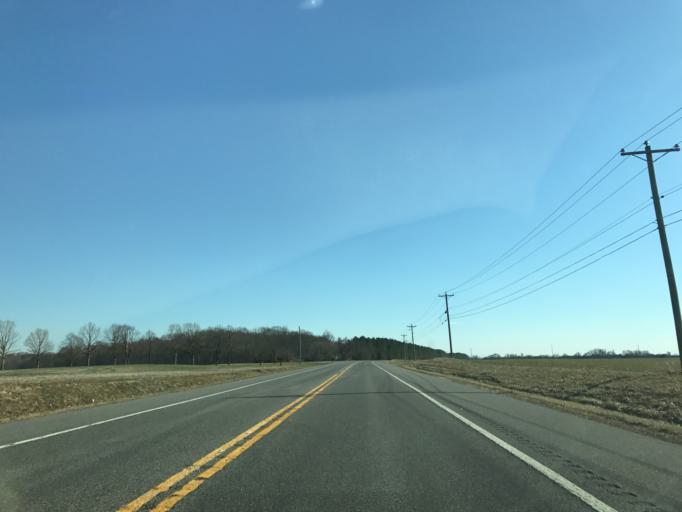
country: US
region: Maryland
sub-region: Queen Anne's County
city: Centreville
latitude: 38.9895
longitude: -76.0741
